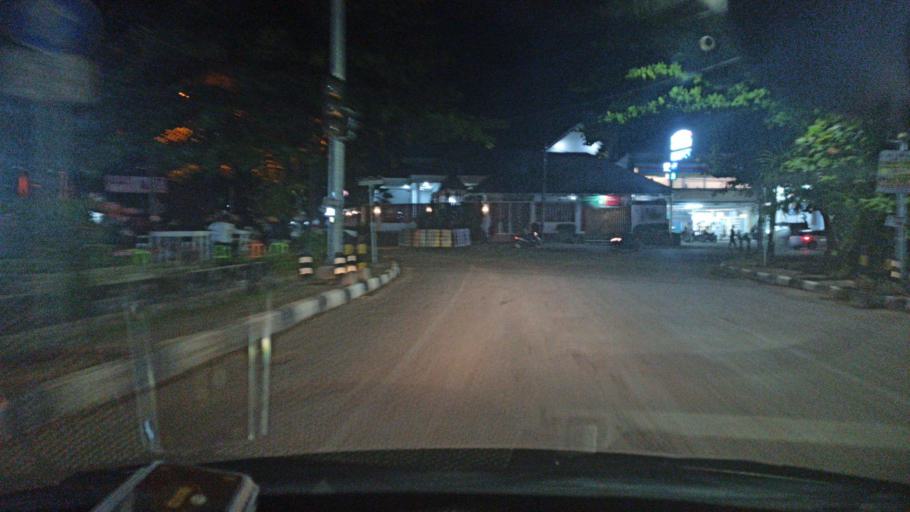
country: ID
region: South Sumatra
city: Plaju
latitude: -2.9897
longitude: 104.7441
